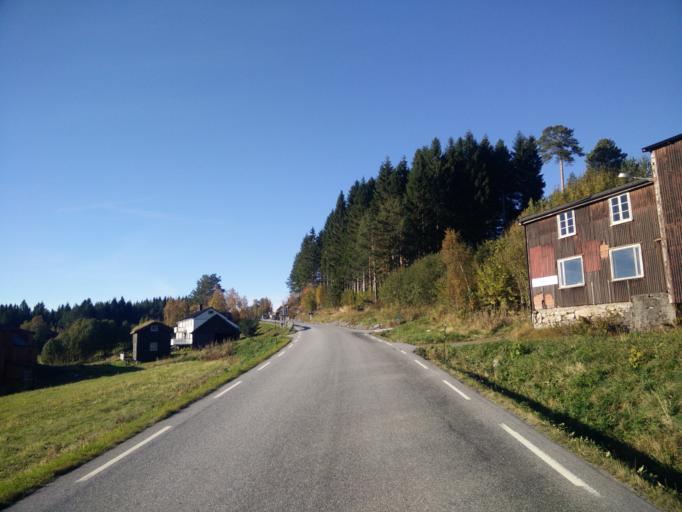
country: NO
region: More og Romsdal
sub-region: Halsa
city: Liaboen
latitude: 63.1166
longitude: 8.3149
